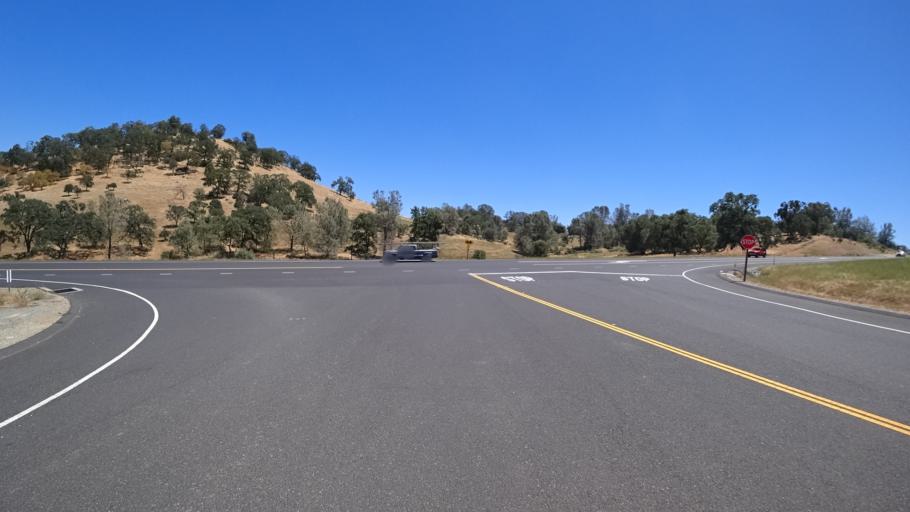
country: US
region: California
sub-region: Calaveras County
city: Copperopolis
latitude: 38.0447
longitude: -120.6472
